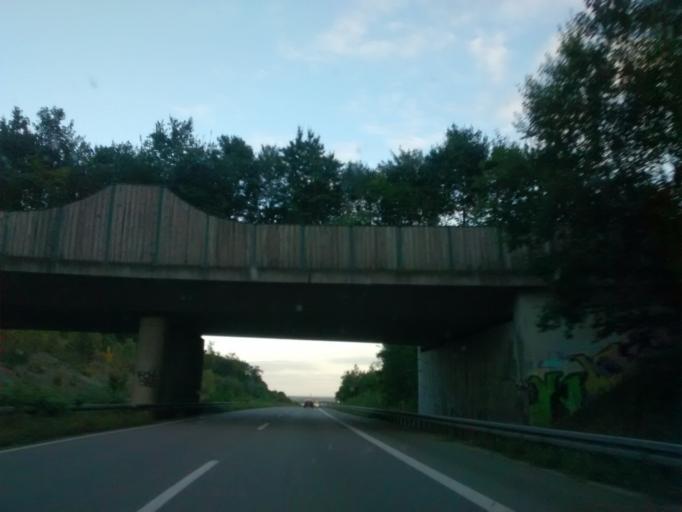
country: DE
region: Lower Saxony
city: Bad Rothenfelde
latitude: 52.1350
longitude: 8.1679
